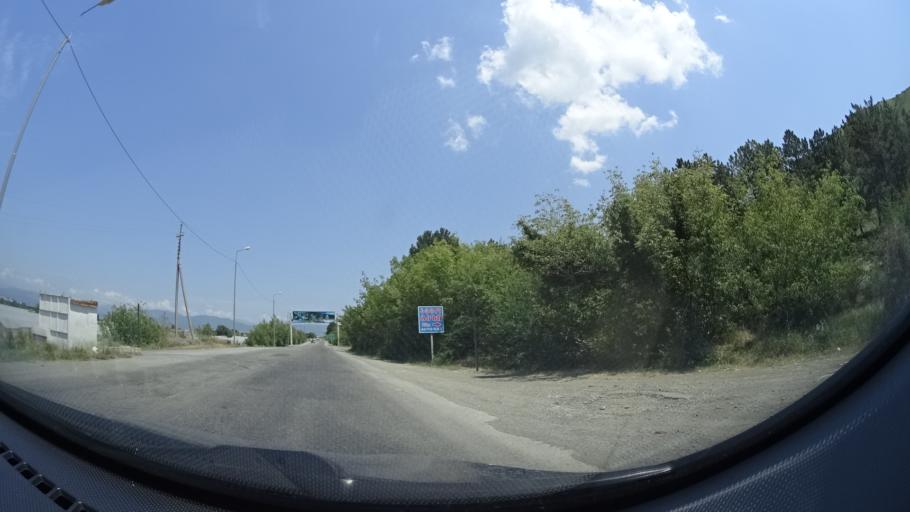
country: GE
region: Shida Kartli
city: Gori
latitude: 42.0131
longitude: 44.1360
